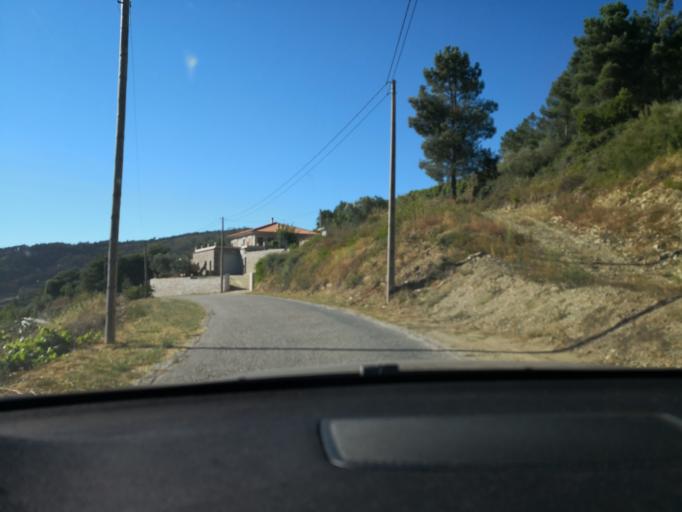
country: PT
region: Vila Real
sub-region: Sabrosa
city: Vilela
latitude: 41.2211
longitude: -7.5801
